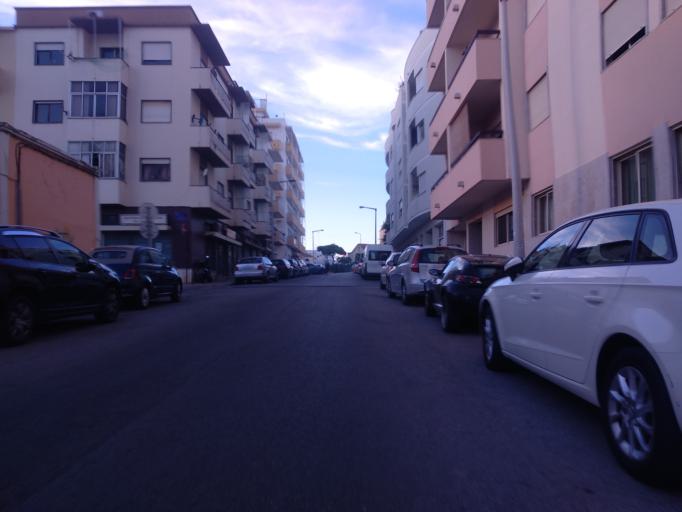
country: PT
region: Faro
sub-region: Faro
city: Faro
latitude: 37.0182
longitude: -7.9253
